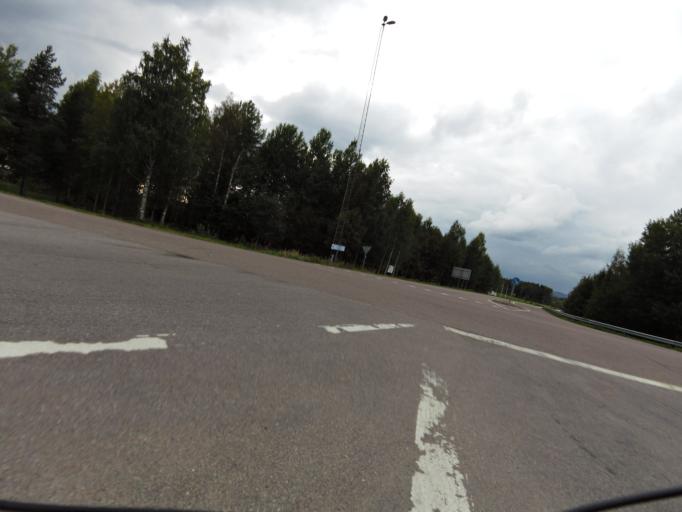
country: SE
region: Gaevleborg
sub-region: Ockelbo Kommun
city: Ockelbo
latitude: 60.9054
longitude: 16.7275
